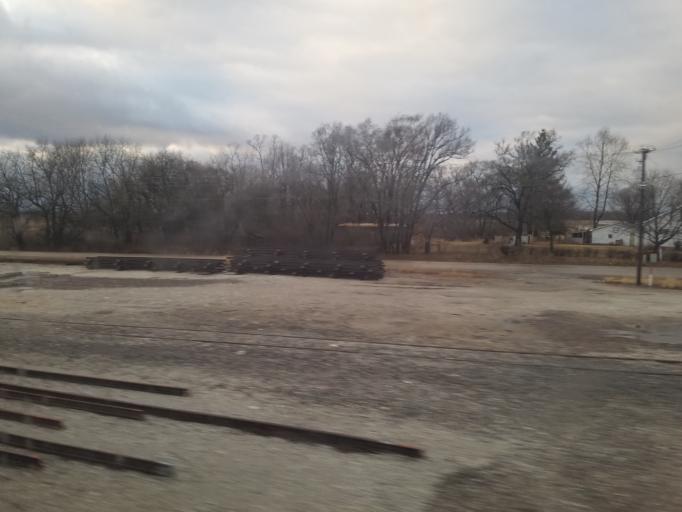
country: US
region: Illinois
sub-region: Henderson County
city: Oquawka
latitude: 40.8656
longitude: -90.9579
